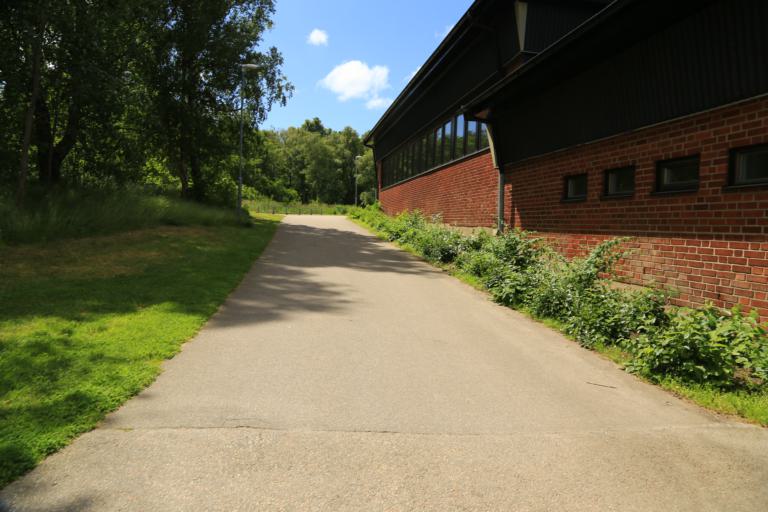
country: SE
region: Halland
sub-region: Varbergs Kommun
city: Varberg
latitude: 57.1189
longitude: 12.2782
